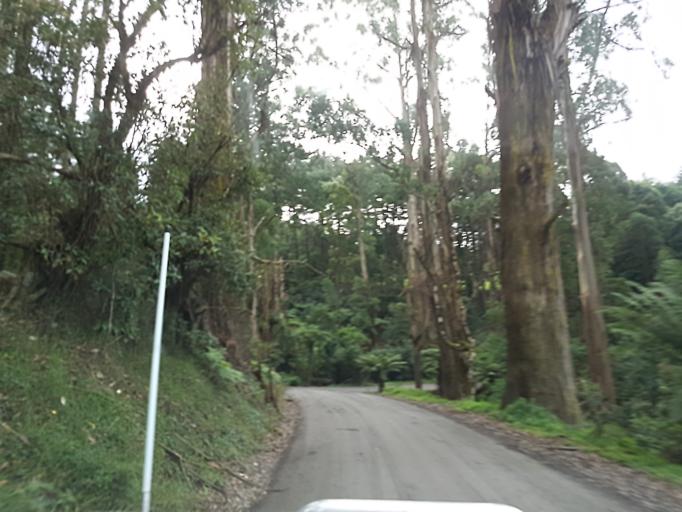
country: AU
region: Victoria
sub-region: Yarra Ranges
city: Monbulk
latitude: -37.8776
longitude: 145.3894
